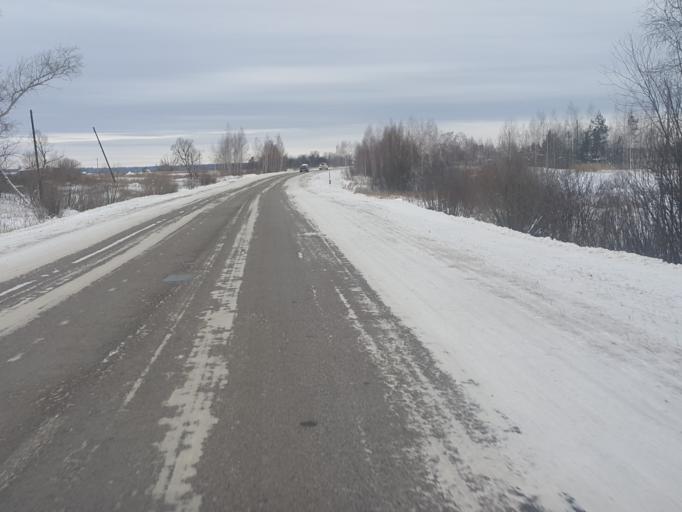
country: RU
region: Tambov
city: Platonovka
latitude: 52.8569
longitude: 41.8312
